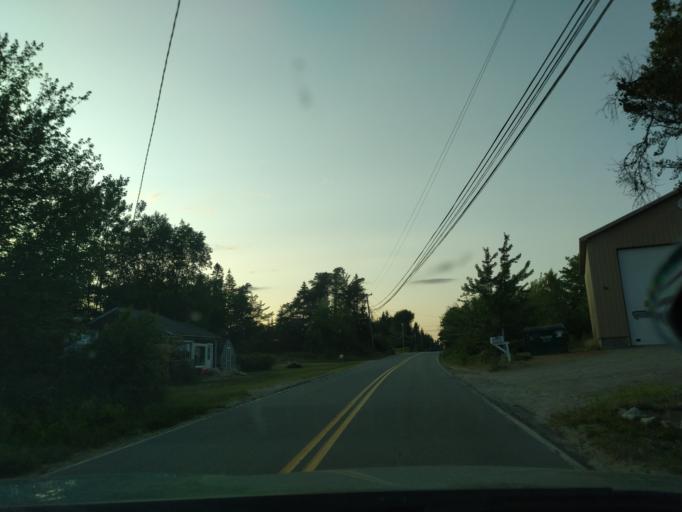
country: US
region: Maine
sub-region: Hancock County
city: Gouldsboro
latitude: 44.3734
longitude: -68.0345
